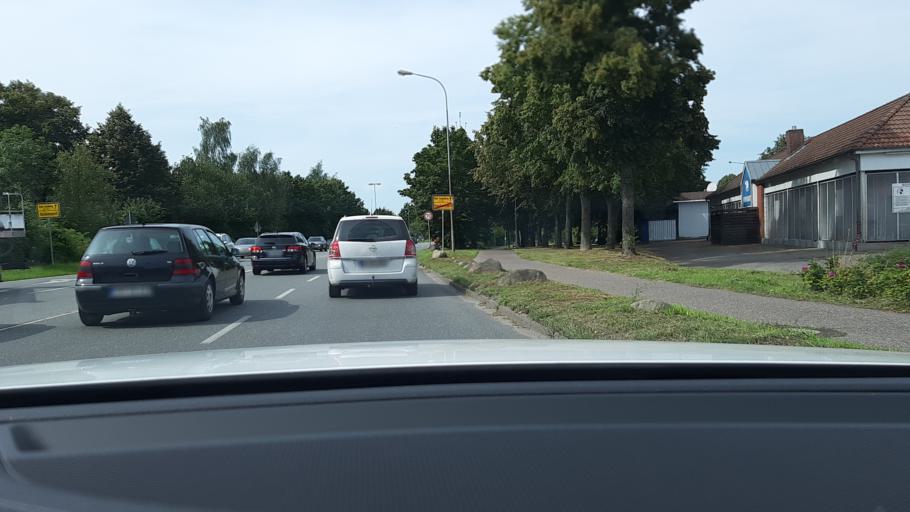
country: DE
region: Schleswig-Holstein
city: Stockelsdorf
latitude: 53.8888
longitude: 10.6411
